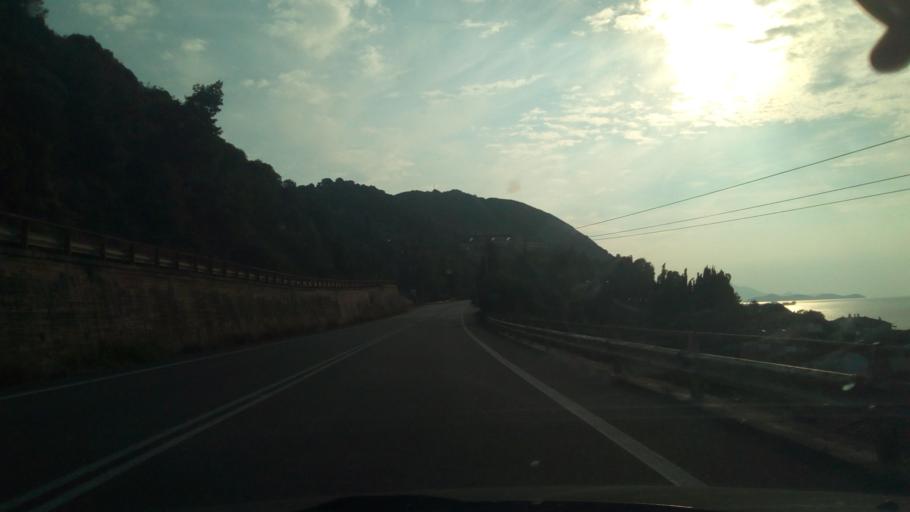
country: GR
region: West Greece
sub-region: Nomos Aitolias kai Akarnanias
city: Nafpaktos
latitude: 38.4083
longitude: 21.9436
